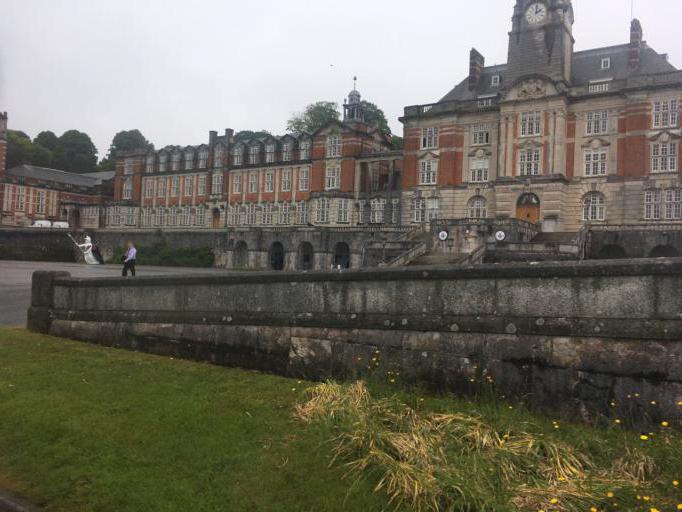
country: GB
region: England
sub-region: Devon
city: Dartmouth
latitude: 50.3566
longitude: -3.5815
